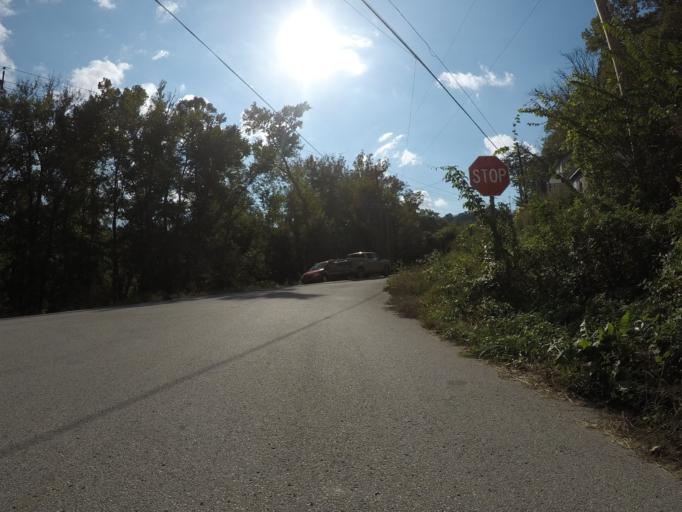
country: US
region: West Virginia
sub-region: Wayne County
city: Lavalette
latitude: 38.3499
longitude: -82.4943
